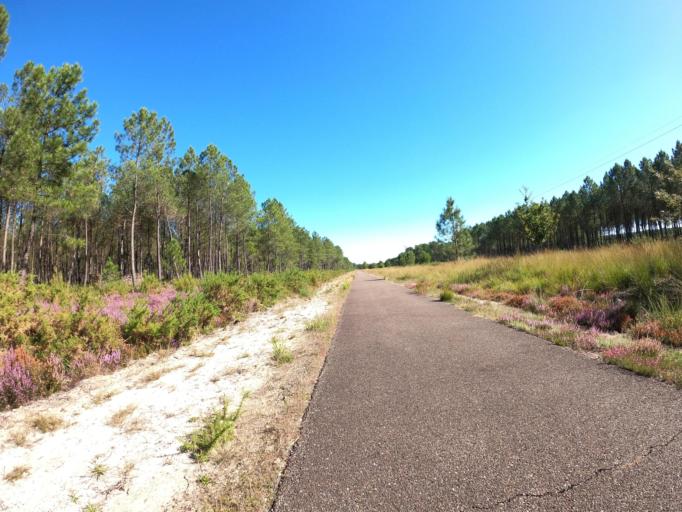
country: FR
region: Aquitaine
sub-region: Departement des Landes
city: Ychoux
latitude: 44.3397
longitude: -0.9638
